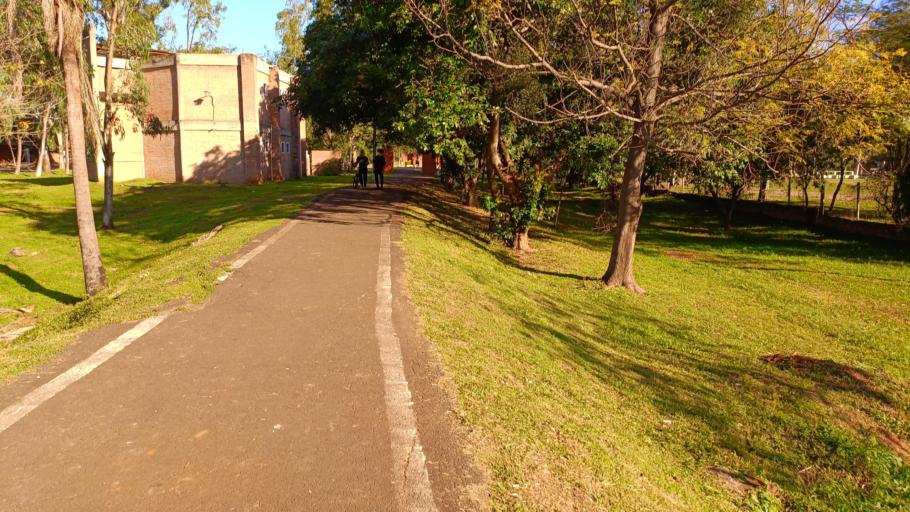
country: PY
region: Itapua
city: Carmen del Parana
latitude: -27.1583
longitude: -56.2404
